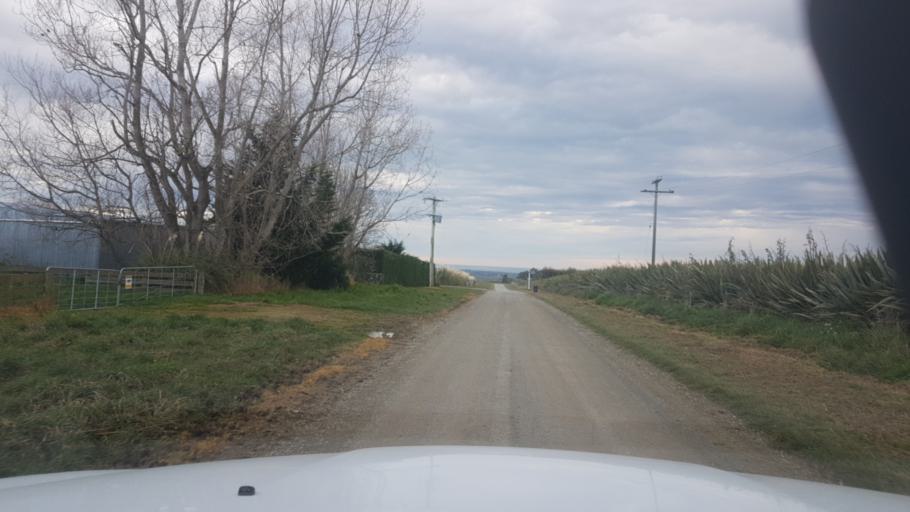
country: NZ
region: Canterbury
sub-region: Timaru District
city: Pleasant Point
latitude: -44.3460
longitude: 171.1220
